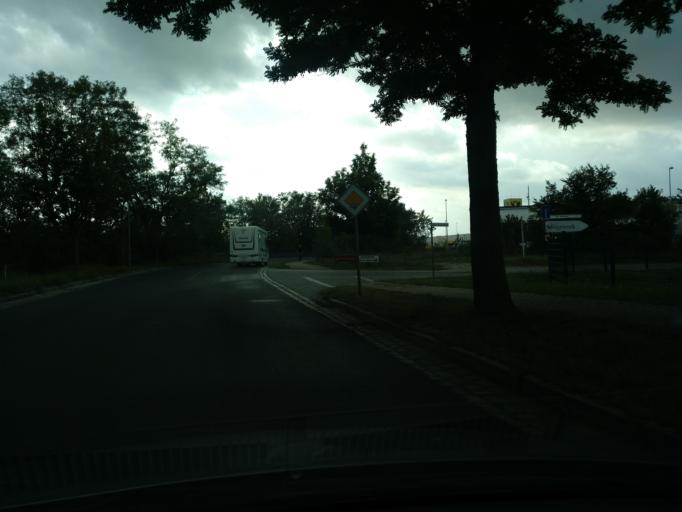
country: DE
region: Brandenburg
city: Petershagen
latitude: 52.4868
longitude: 13.7823
